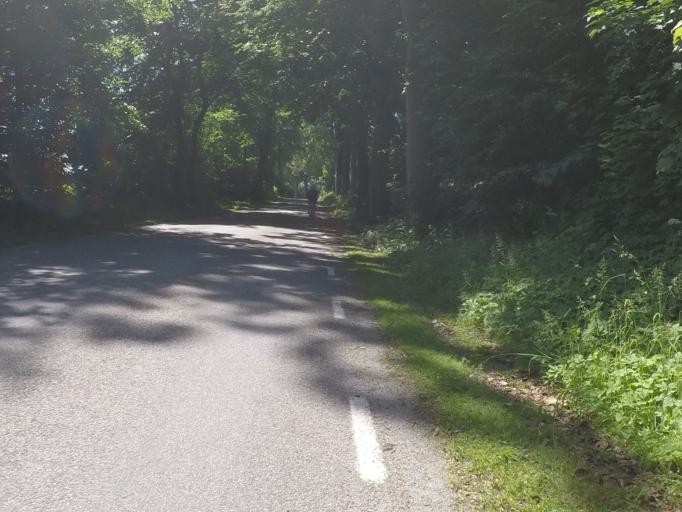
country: SE
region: Skane
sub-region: Svedala Kommun
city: Klagerup
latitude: 55.5643
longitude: 13.2130
